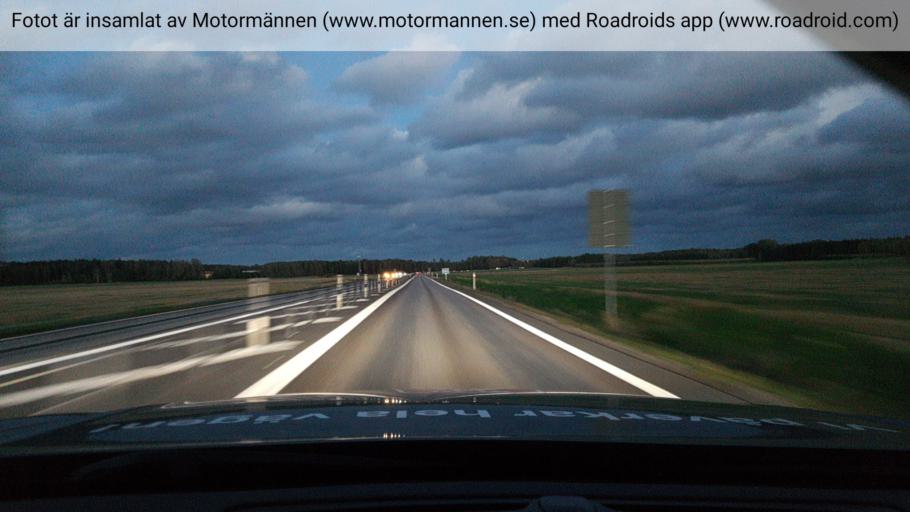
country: SE
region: Vaermland
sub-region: Kristinehamns Kommun
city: Kristinehamn
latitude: 59.3747
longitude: 13.9806
